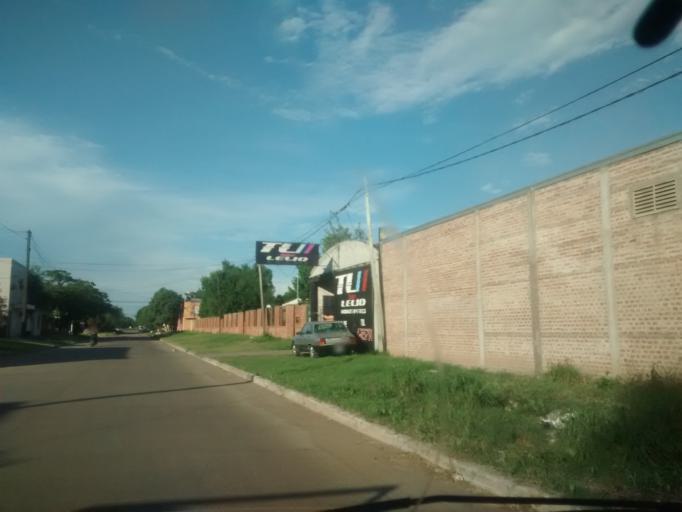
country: AR
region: Chaco
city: Fontana
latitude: -27.4438
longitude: -59.0087
